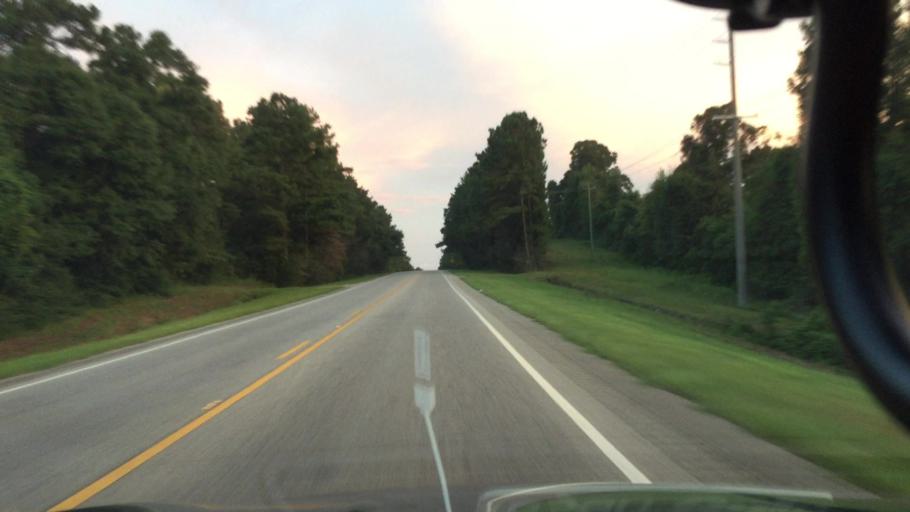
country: US
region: Alabama
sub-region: Coffee County
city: Enterprise
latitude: 31.3704
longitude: -85.8697
